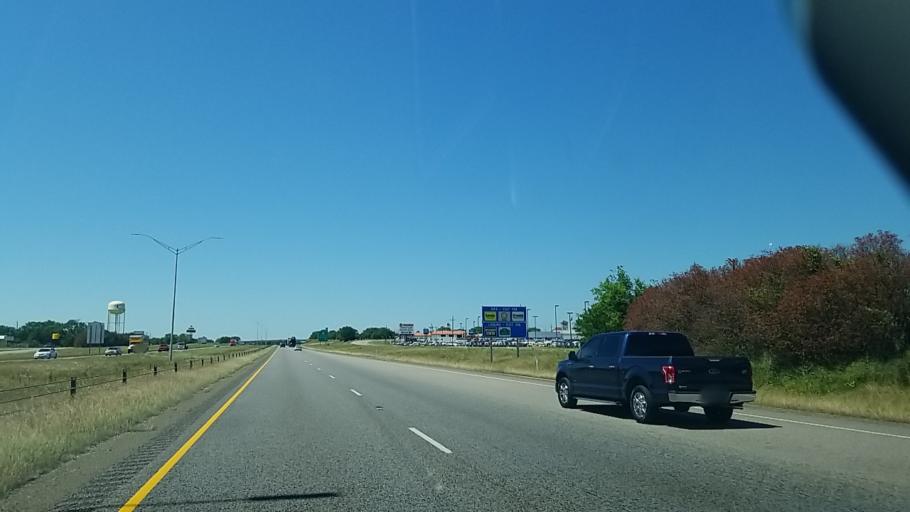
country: US
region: Texas
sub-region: Freestone County
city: Fairfield
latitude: 31.7193
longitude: -96.1779
